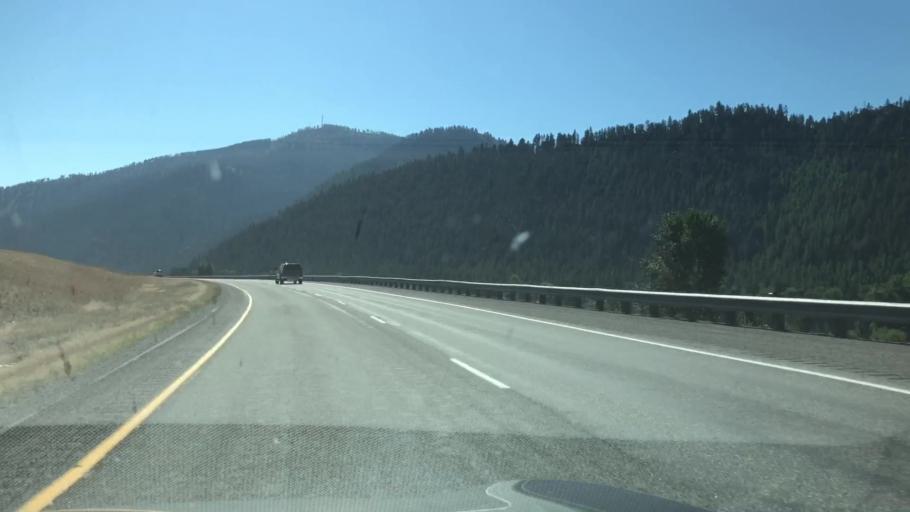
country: US
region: Montana
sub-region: Missoula County
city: Clinton
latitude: 46.7063
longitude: -113.5059
